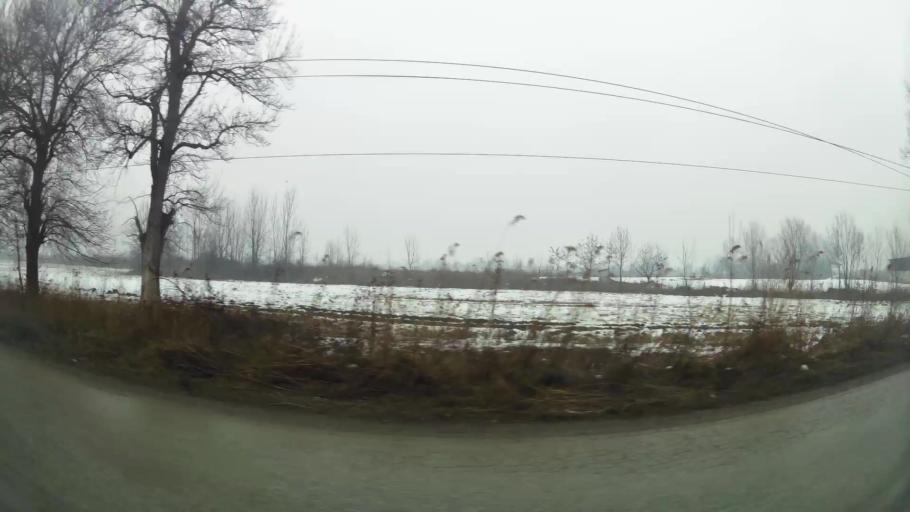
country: MK
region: Petrovec
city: Petrovec
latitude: 41.9438
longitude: 21.6029
